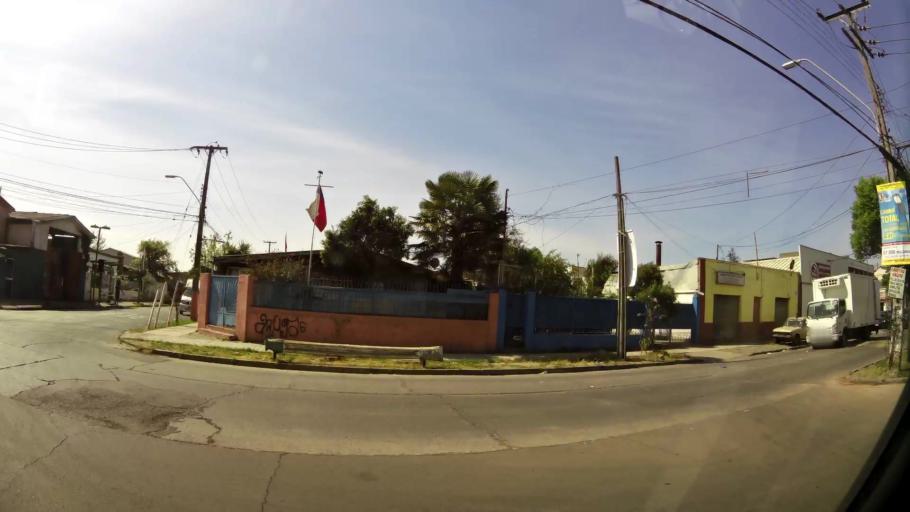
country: CL
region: Santiago Metropolitan
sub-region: Provincia de Maipo
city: San Bernardo
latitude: -33.5370
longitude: -70.6758
